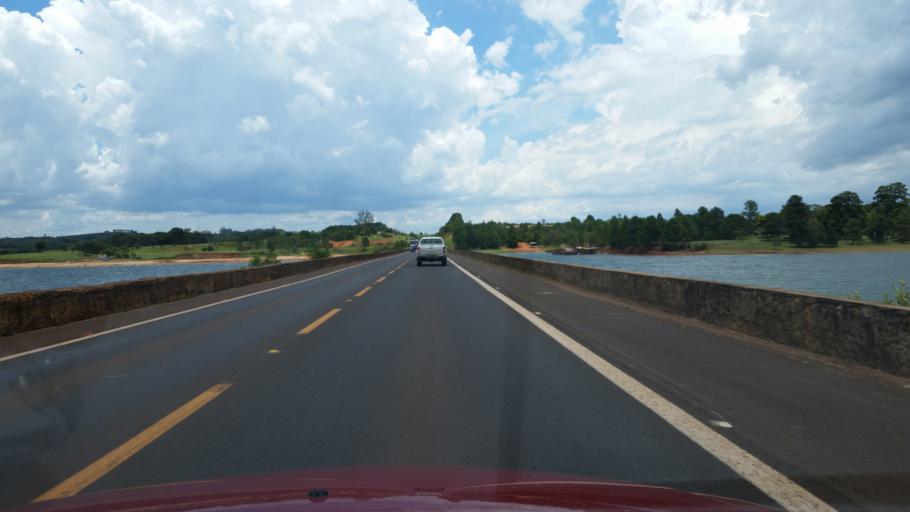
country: BR
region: Sao Paulo
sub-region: Itai
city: Itai
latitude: -23.2706
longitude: -49.0128
